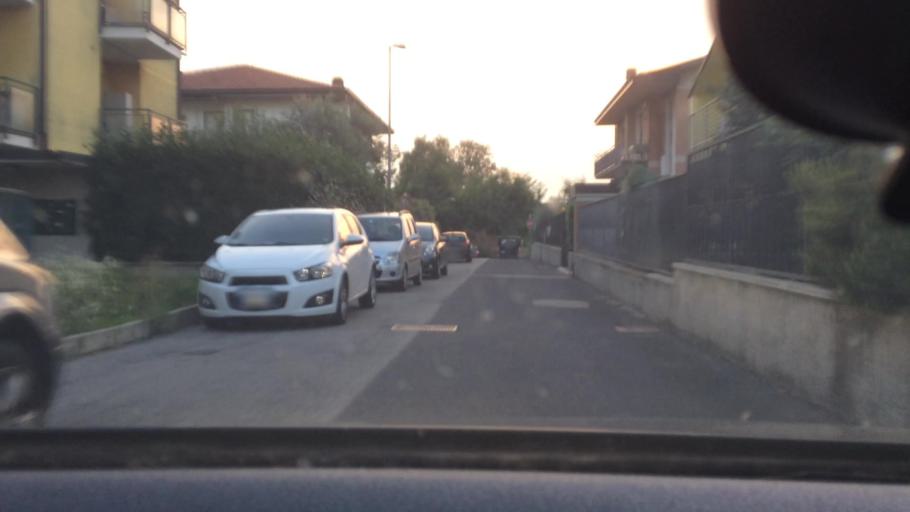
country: IT
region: Lombardy
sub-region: Provincia di Como
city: Turate
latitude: 45.6507
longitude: 8.9977
